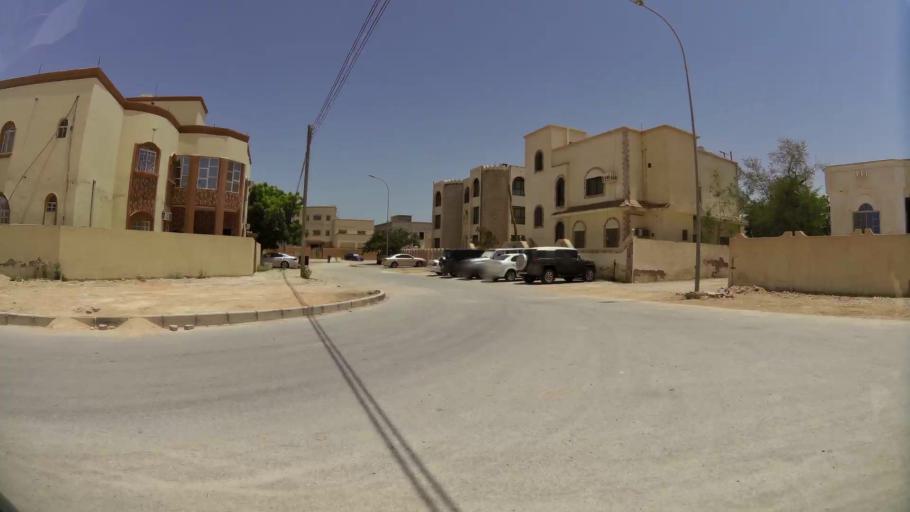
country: OM
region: Zufar
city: Salalah
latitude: 17.0721
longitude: 54.1584
